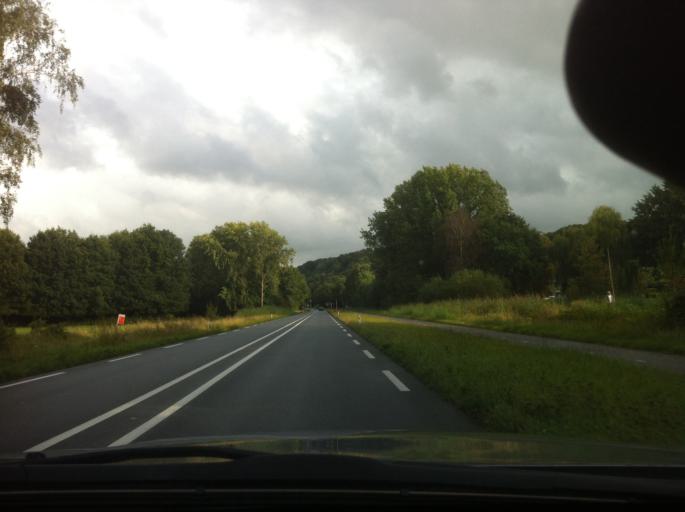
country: NL
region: Gelderland
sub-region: Gemeente Groesbeek
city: Berg en Dal
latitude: 51.8279
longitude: 5.9373
